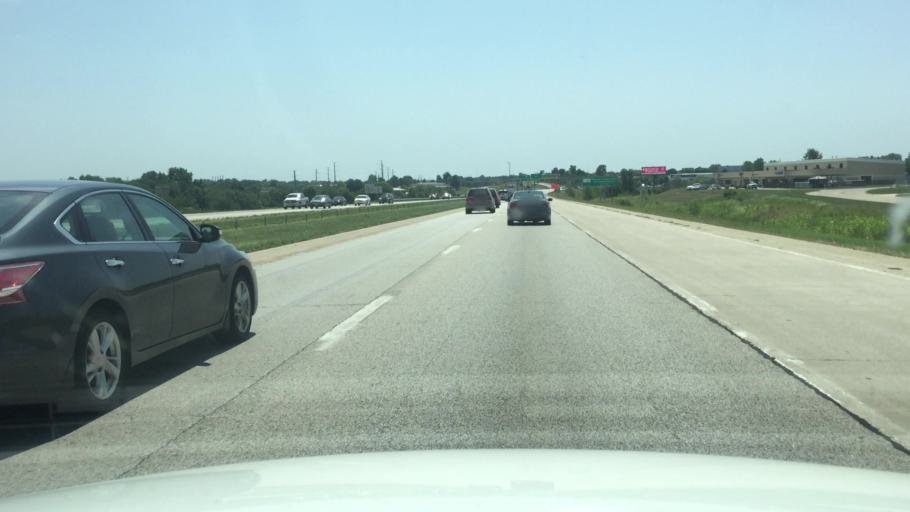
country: US
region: Missouri
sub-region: Jackson County
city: Lees Summit
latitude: 38.9565
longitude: -94.3603
